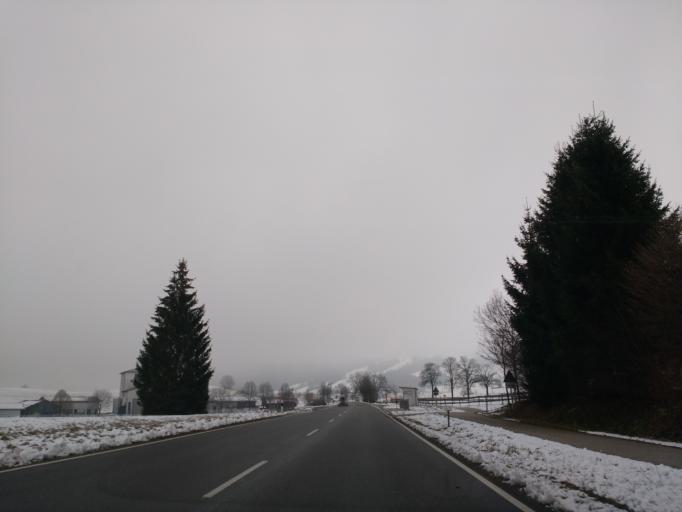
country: DE
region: Bavaria
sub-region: Swabia
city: Nesselwang
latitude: 47.6296
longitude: 10.4840
